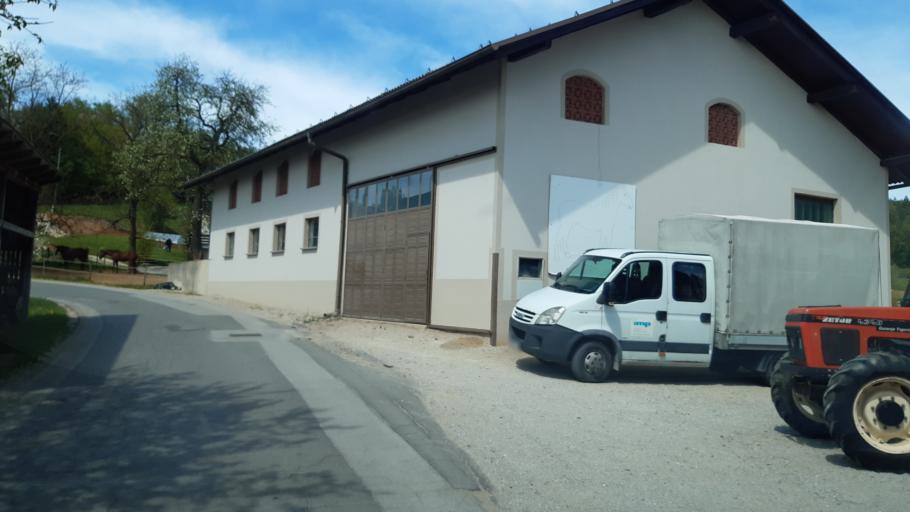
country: SI
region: Lukovica
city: Lukovica pri Domzalah
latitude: 46.1750
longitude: 14.6739
